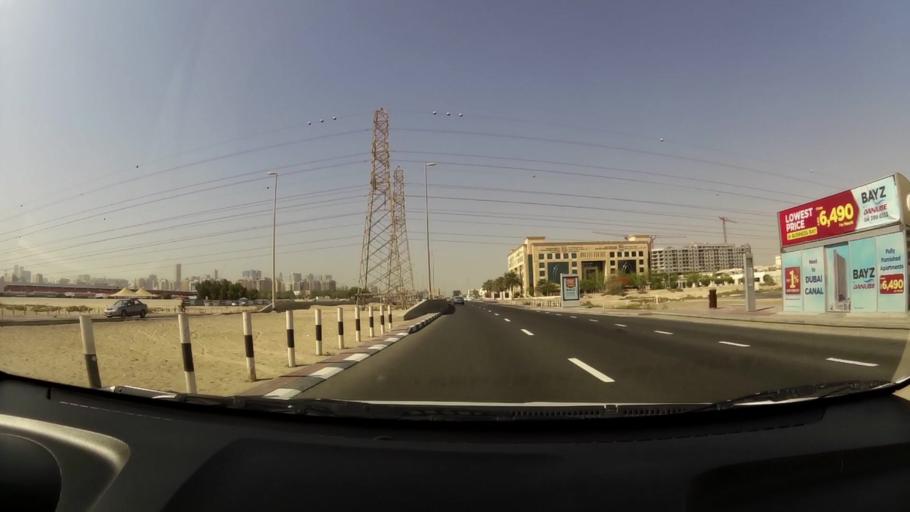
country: AE
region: Ash Shariqah
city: Sharjah
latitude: 25.2788
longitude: 55.3766
